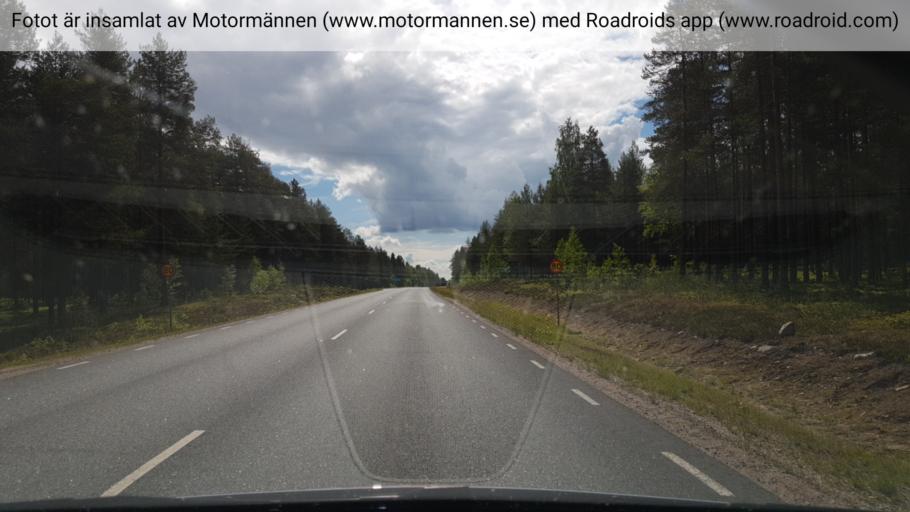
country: FI
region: Lapland
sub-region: Torniolaakso
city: Ylitornio
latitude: 66.2975
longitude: 23.6362
